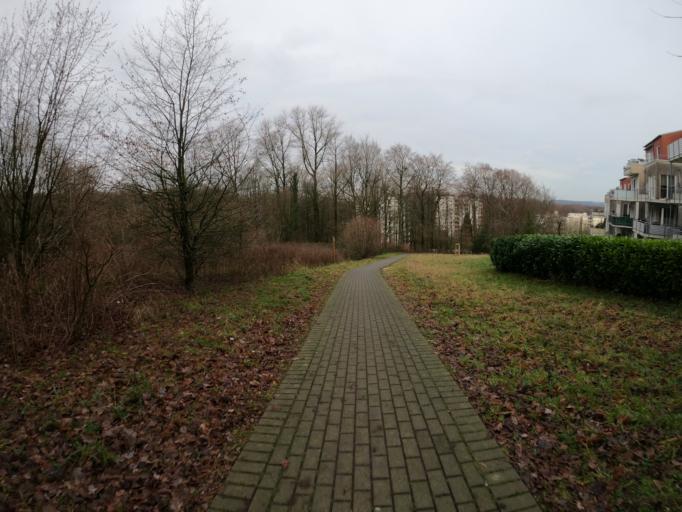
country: DE
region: North Rhine-Westphalia
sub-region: Regierungsbezirk Dusseldorf
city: Wuppertal
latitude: 51.2325
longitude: 7.1400
